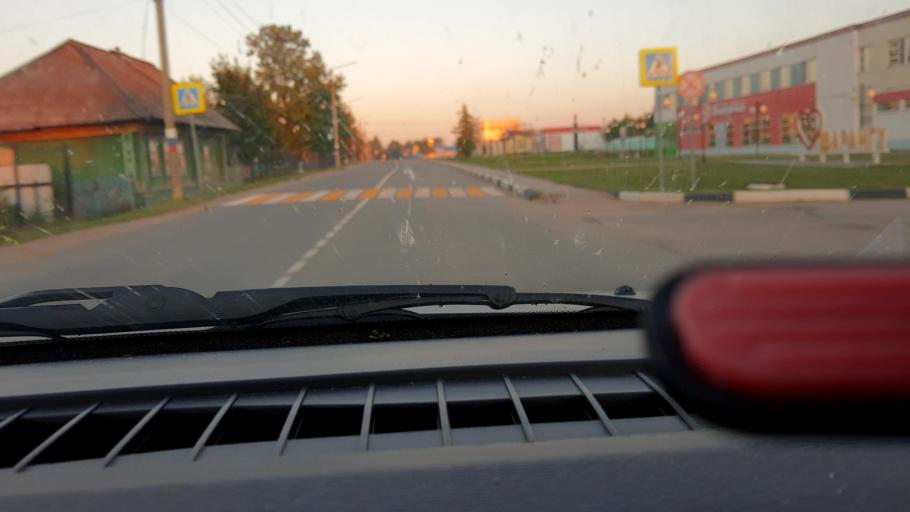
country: RU
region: Nizjnij Novgorod
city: Sharanga
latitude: 57.1834
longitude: 46.5359
